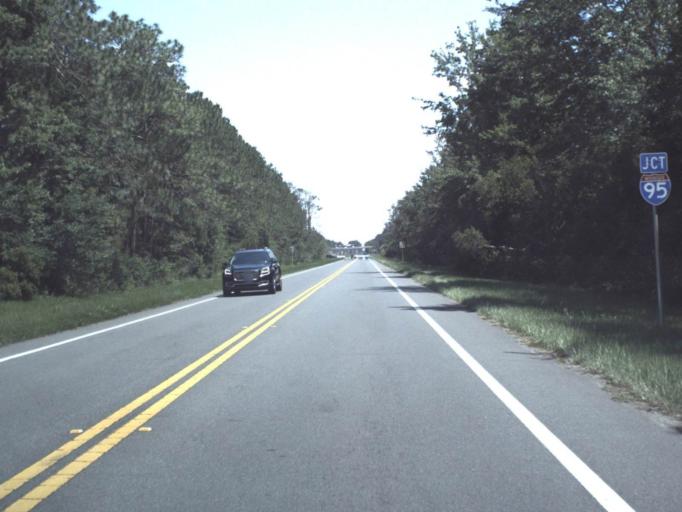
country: US
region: Georgia
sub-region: Camden County
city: Kingsland
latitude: 30.7196
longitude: -81.6779
